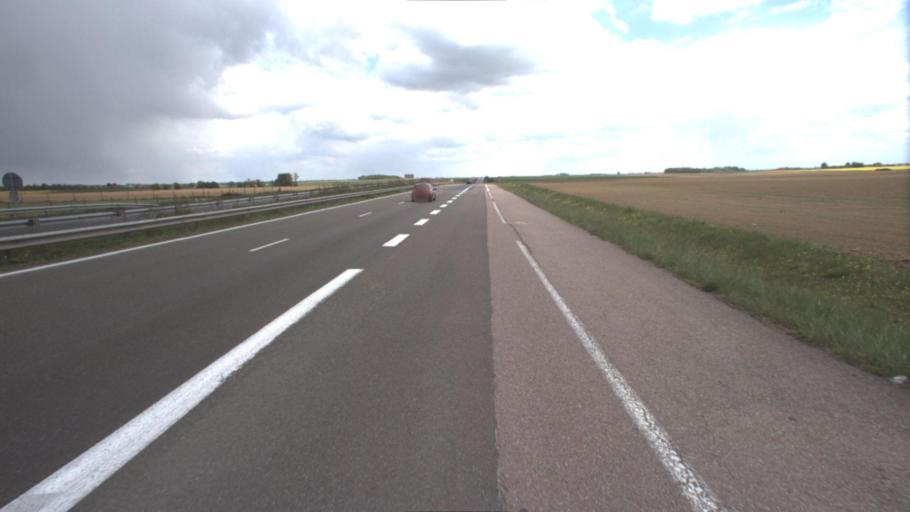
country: FR
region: Ile-de-France
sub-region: Departement de Seine-et-Marne
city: Touquin
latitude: 48.6855
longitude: 3.0259
